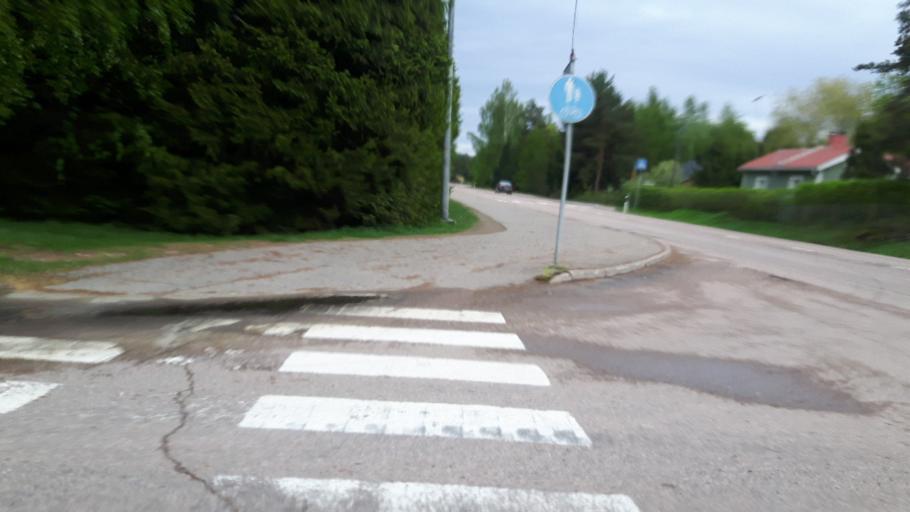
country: FI
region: Kymenlaakso
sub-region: Kotka-Hamina
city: Hamina
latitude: 60.5618
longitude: 27.2233
